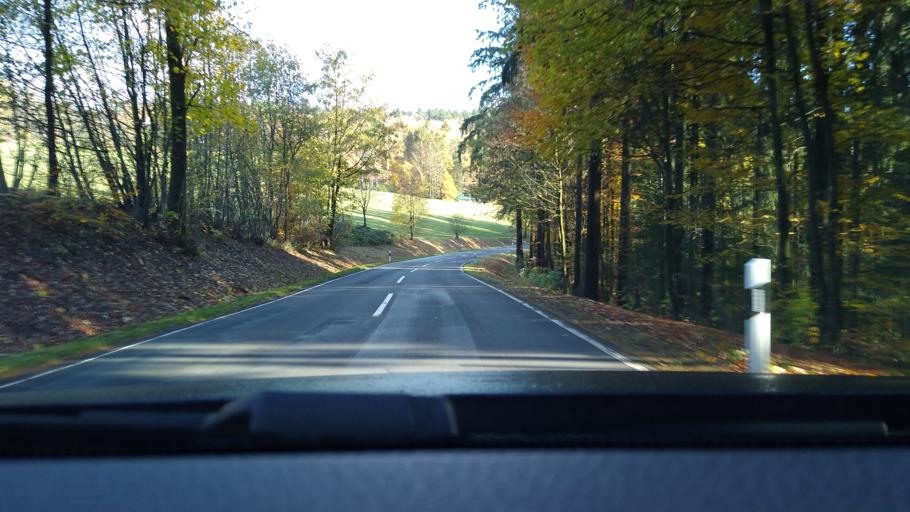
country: DE
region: Hesse
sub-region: Regierungsbezirk Kassel
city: Poppenhausen
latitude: 50.4686
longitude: 9.8728
